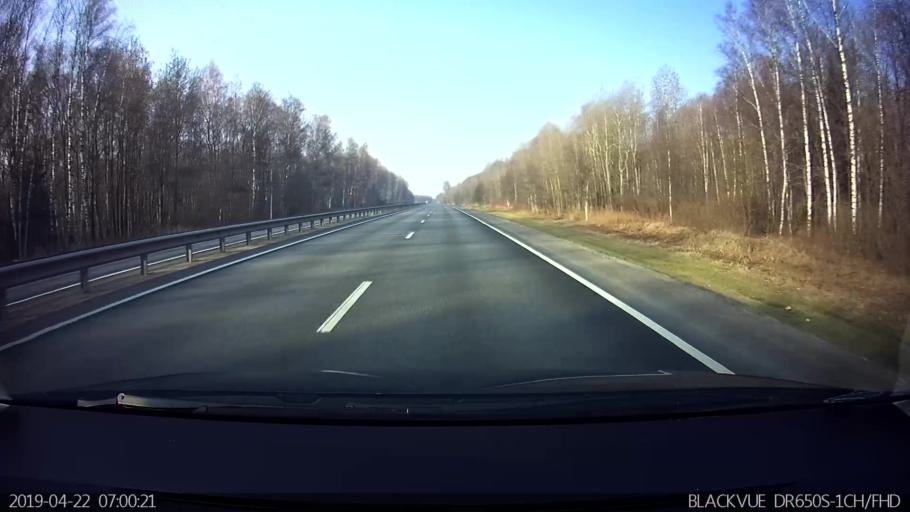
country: RU
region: Smolensk
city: Gagarin
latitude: 55.4184
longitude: 34.7842
